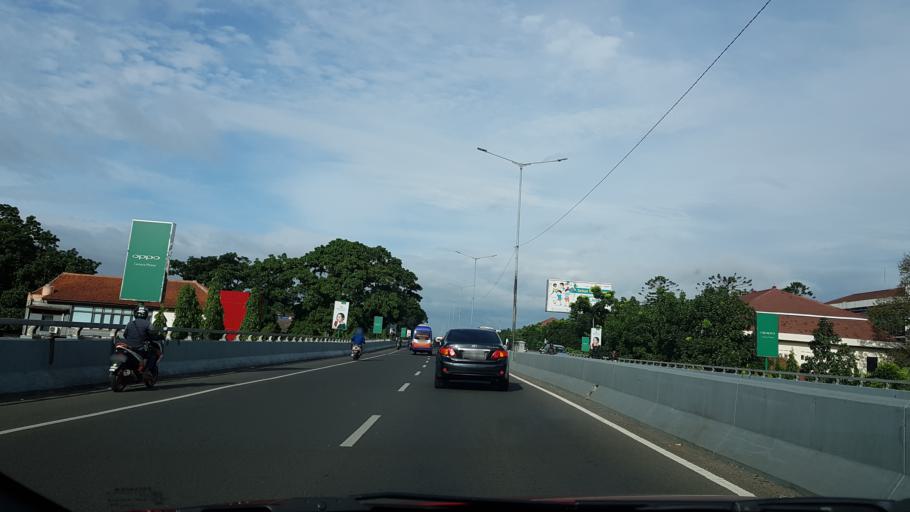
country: ID
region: West Java
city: Bandung
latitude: -6.9003
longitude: 107.6025
